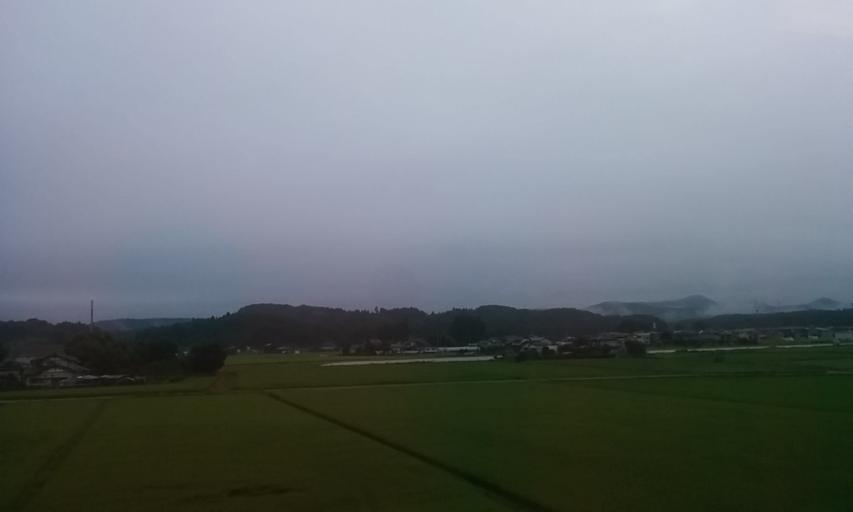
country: JP
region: Tochigi
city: Utsunomiya-shi
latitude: 36.6312
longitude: 139.9094
